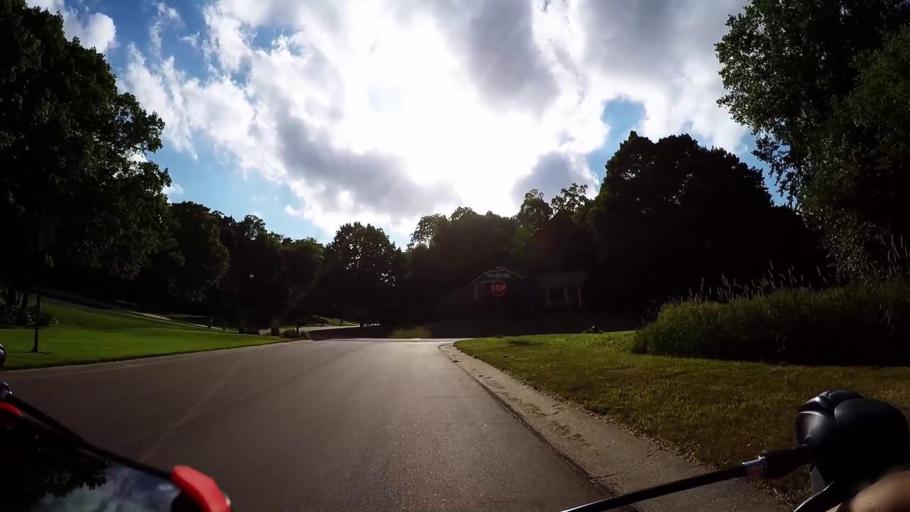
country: US
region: Minnesota
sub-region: Hennepin County
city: Minnetonka
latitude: 44.8883
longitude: -93.4881
